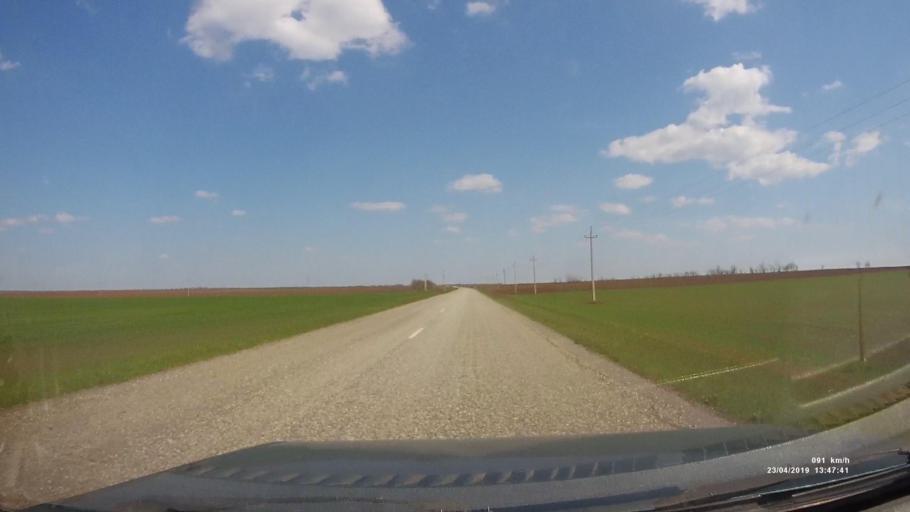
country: RU
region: Kalmykiya
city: Yashalta
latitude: 46.5993
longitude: 42.8585
